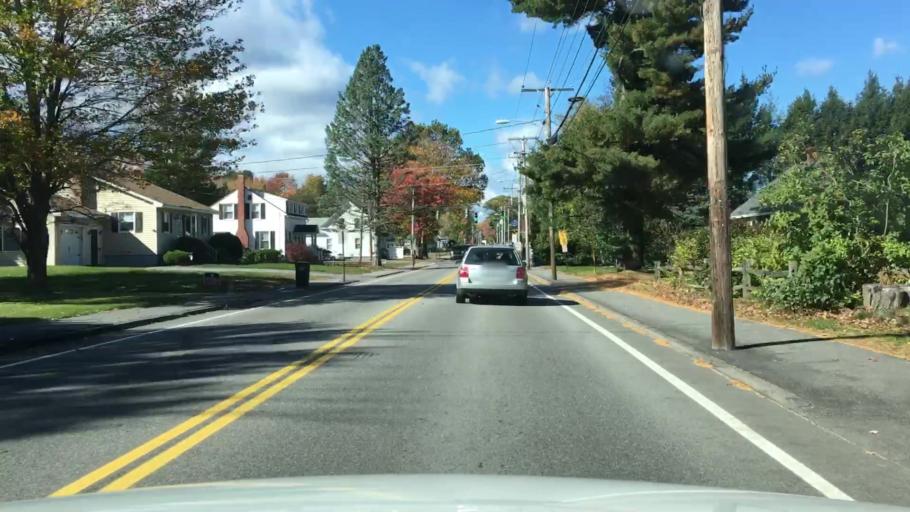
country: US
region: Maine
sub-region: York County
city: Biddeford
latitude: 43.4780
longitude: -70.4622
